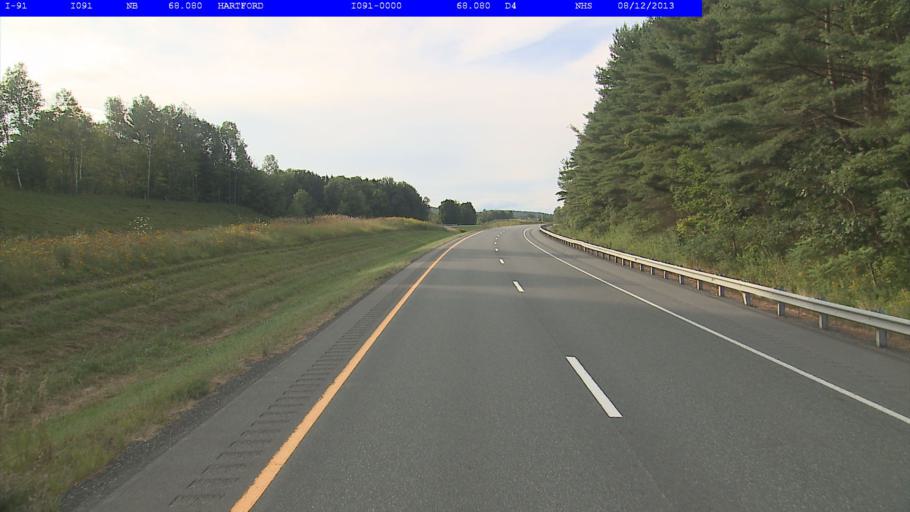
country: US
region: Vermont
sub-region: Windsor County
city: White River Junction
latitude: 43.6160
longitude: -72.3472
